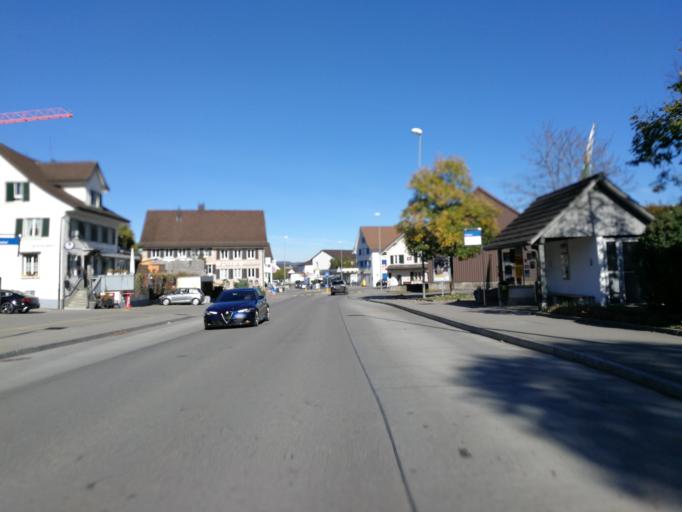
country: CH
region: Zurich
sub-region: Bezirk Hinwil
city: Binzikon
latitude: 47.2777
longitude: 8.7591
